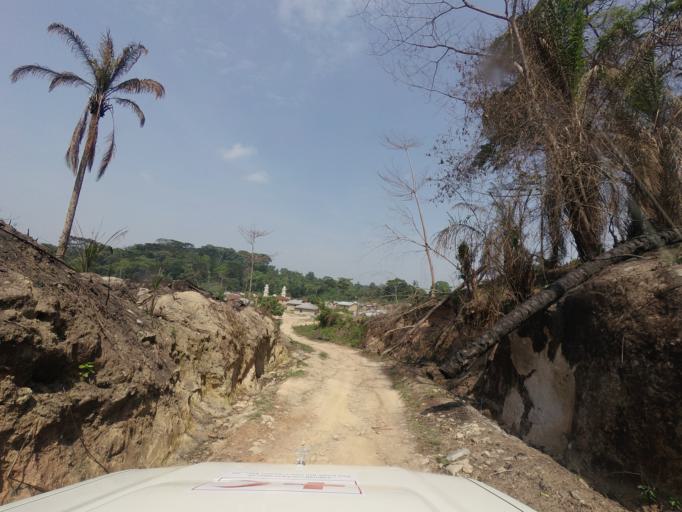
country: LR
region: Lofa
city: Voinjama
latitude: 8.5161
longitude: -9.6269
